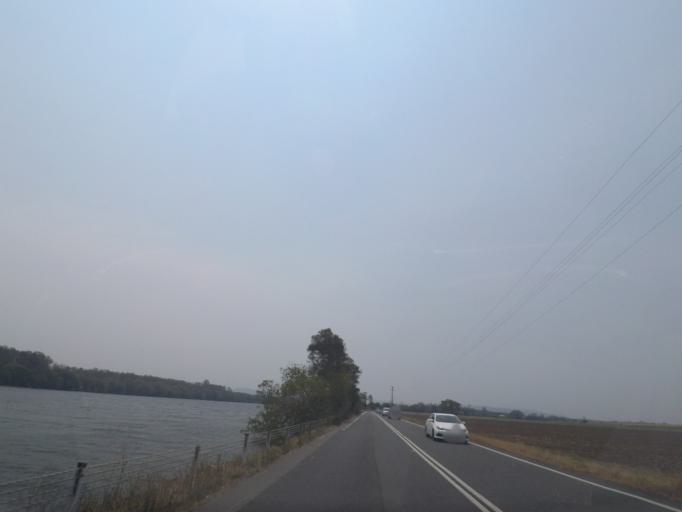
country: AU
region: New South Wales
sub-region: Richmond Valley
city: Evans Head
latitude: -28.9767
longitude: 153.4616
